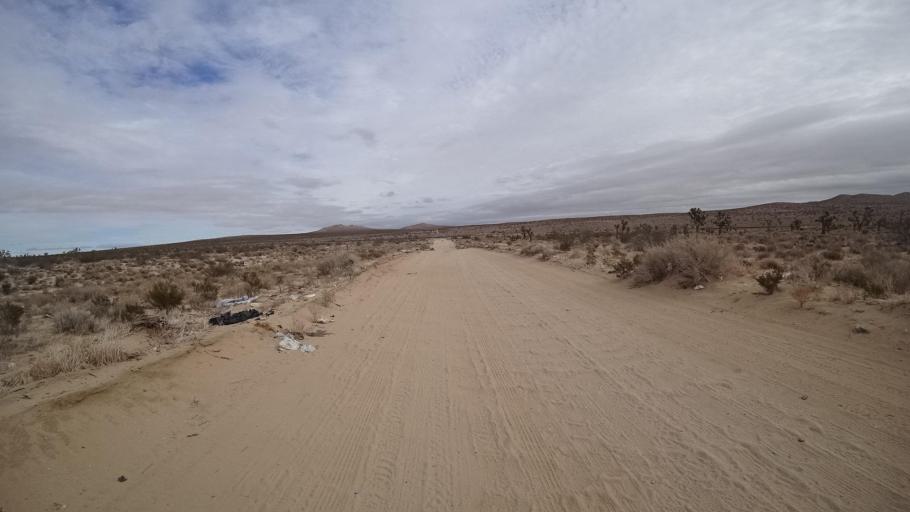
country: US
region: California
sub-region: Kern County
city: Rosamond
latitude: 34.9082
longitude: -118.1566
